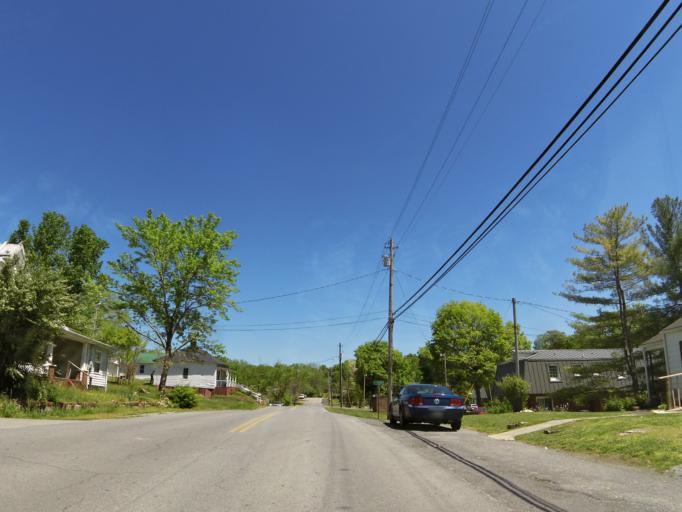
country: US
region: Tennessee
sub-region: Greene County
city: Greeneville
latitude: 36.1554
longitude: -82.8417
